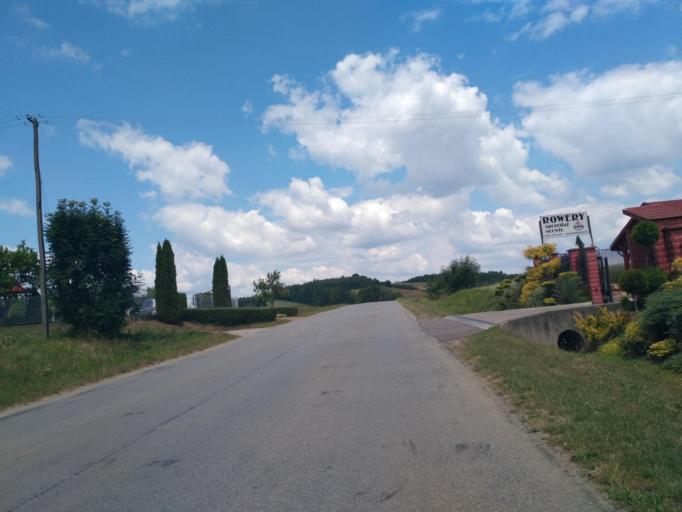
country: PL
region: Subcarpathian Voivodeship
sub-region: Powiat jasielski
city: Brzyska
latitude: 49.8441
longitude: 21.3868
